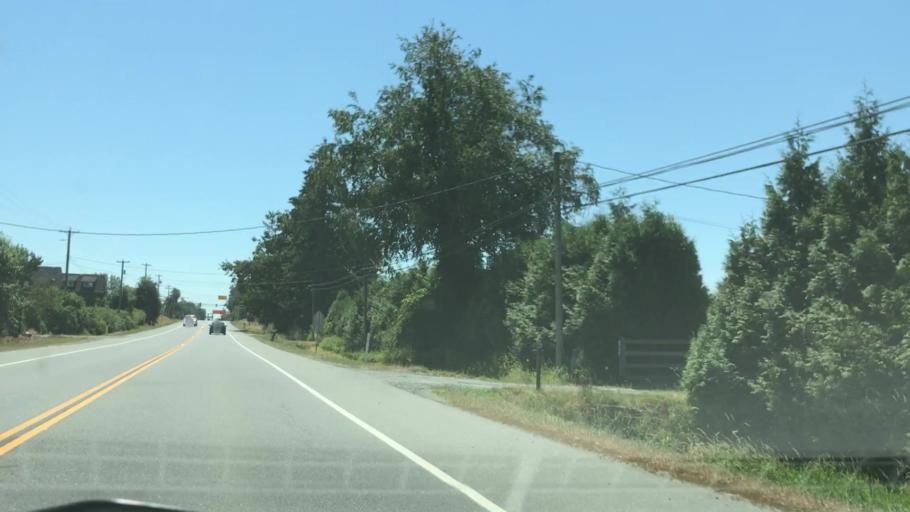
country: CA
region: British Columbia
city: Aldergrove
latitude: 49.0347
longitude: -122.4926
